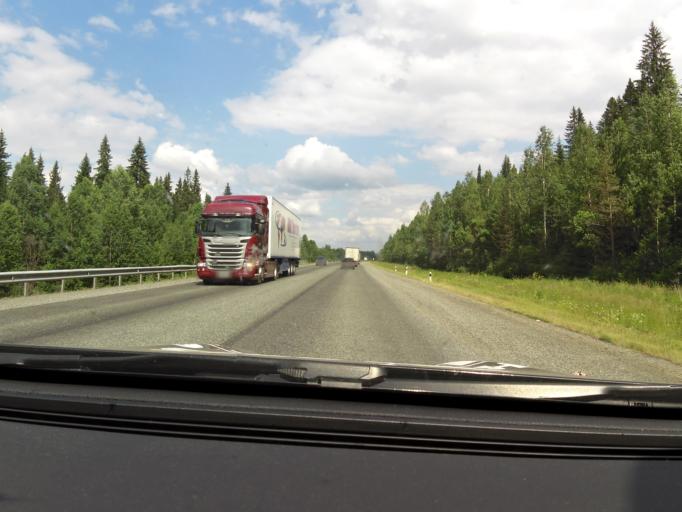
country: RU
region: Sverdlovsk
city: Arti
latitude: 56.7887
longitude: 58.4380
